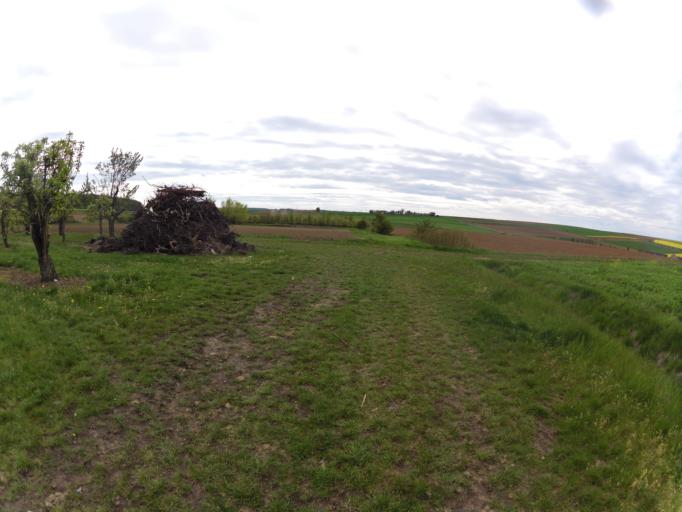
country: DE
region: Bavaria
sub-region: Regierungsbezirk Unterfranken
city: Prosselsheim
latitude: 49.8660
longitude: 10.1544
